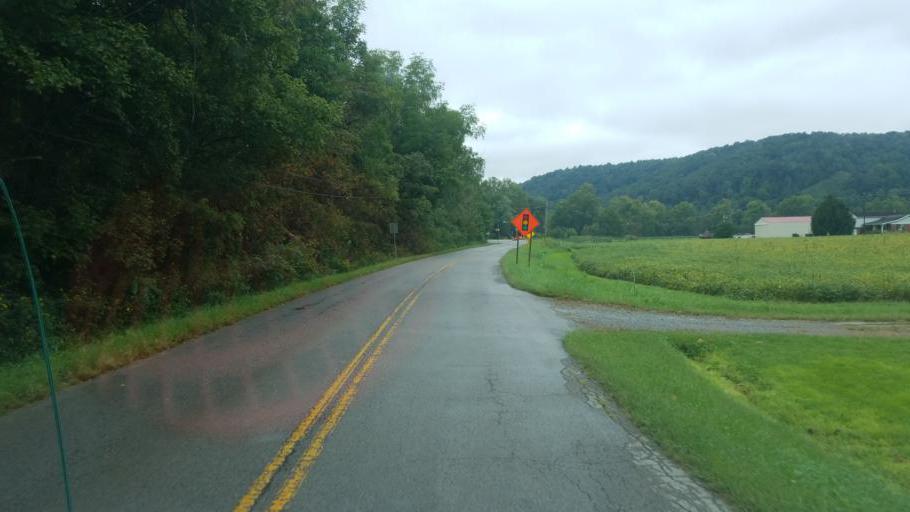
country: US
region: Kentucky
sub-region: Rowan County
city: Morehead
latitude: 38.3465
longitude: -83.5310
